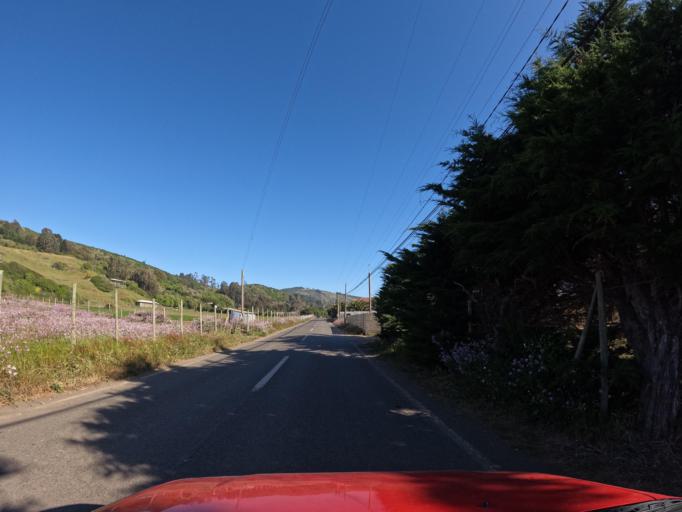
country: CL
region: Maule
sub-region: Provincia de Talca
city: Constitucion
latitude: -34.8423
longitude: -72.1422
